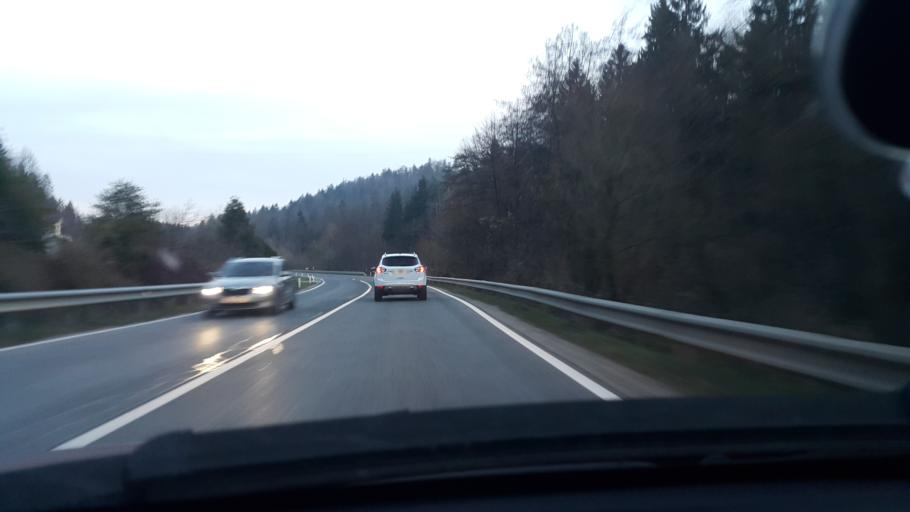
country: SI
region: Velenje
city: Velenje
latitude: 46.3496
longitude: 15.1336
